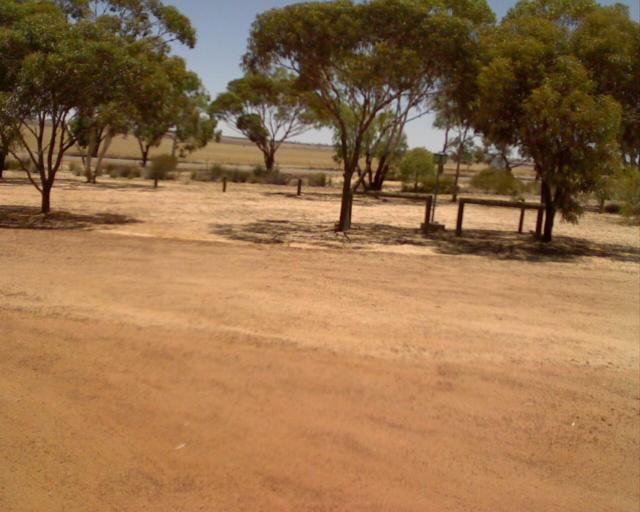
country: AU
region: Western Australia
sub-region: Merredin
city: Merredin
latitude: -30.8184
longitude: 117.8632
